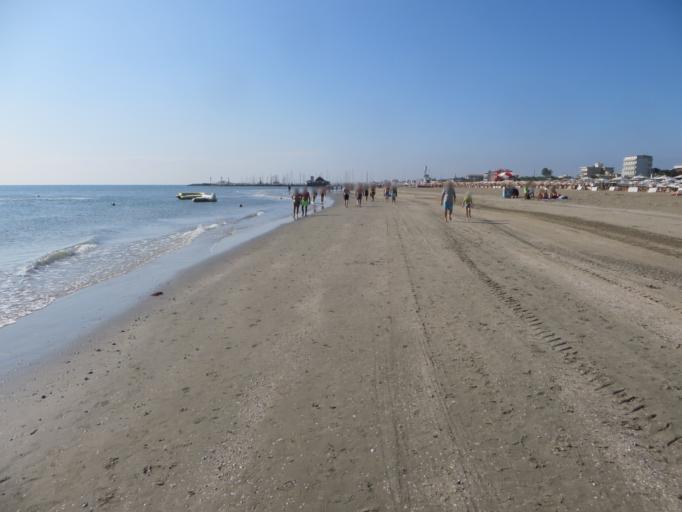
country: IT
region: Emilia-Romagna
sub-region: Provincia di Ravenna
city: Cervia
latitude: 44.2729
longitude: 12.3565
